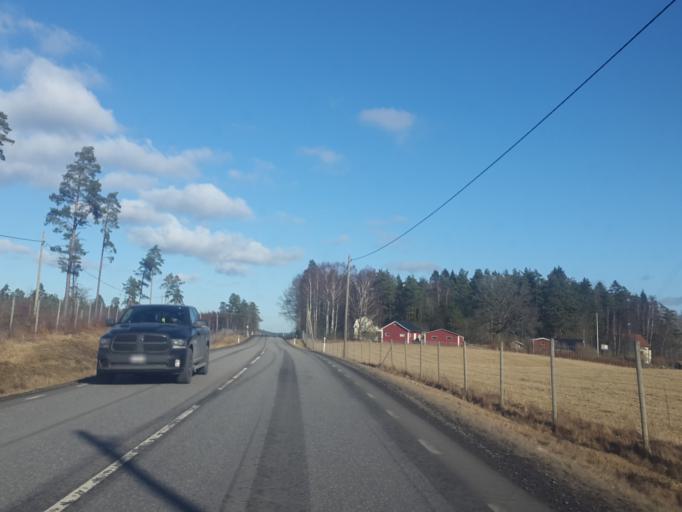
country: SE
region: Vaestra Goetaland
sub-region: Lerums Kommun
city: Grabo
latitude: 57.9335
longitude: 12.3768
